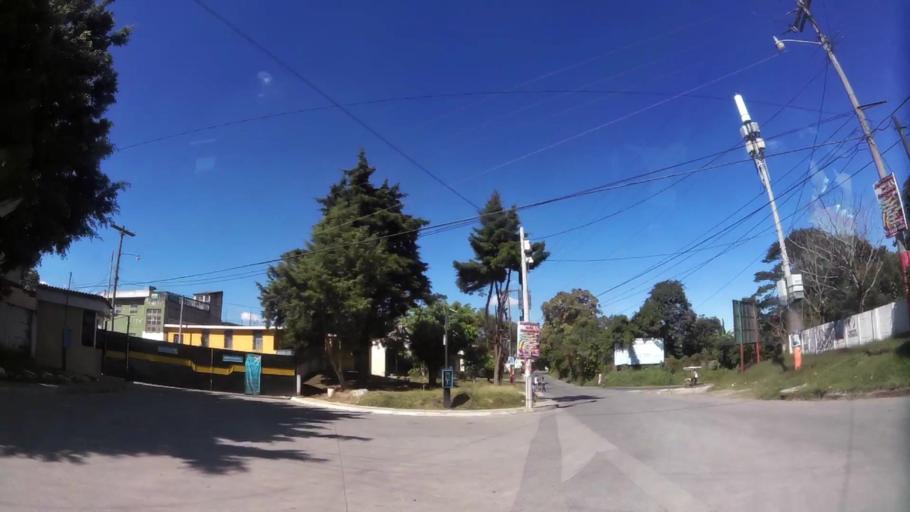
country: GT
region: Guatemala
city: Petapa
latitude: 14.4972
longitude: -90.5631
